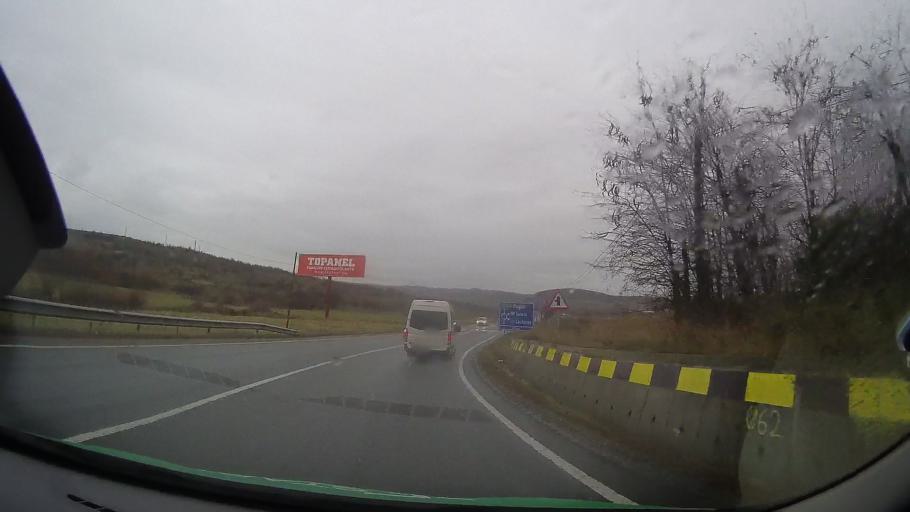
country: RO
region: Bistrita-Nasaud
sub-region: Comuna Galatii Bistritei
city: Galatii Bistritei
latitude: 47.0124
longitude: 24.4075
